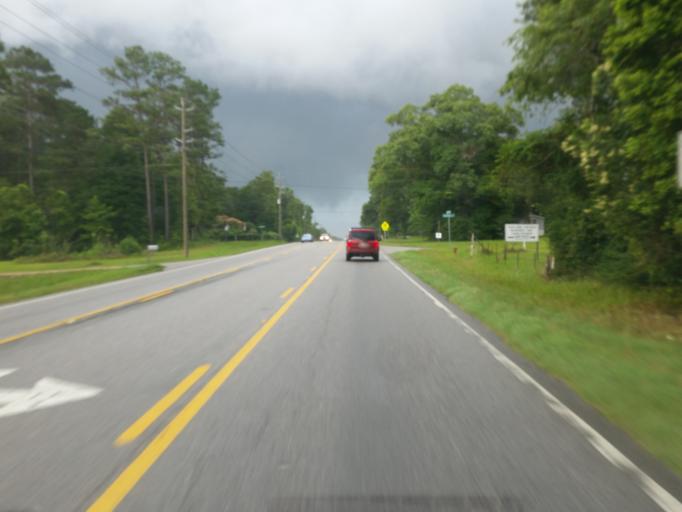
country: US
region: Alabama
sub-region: Mobile County
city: Chickasaw
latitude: 30.7905
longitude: -88.2981
